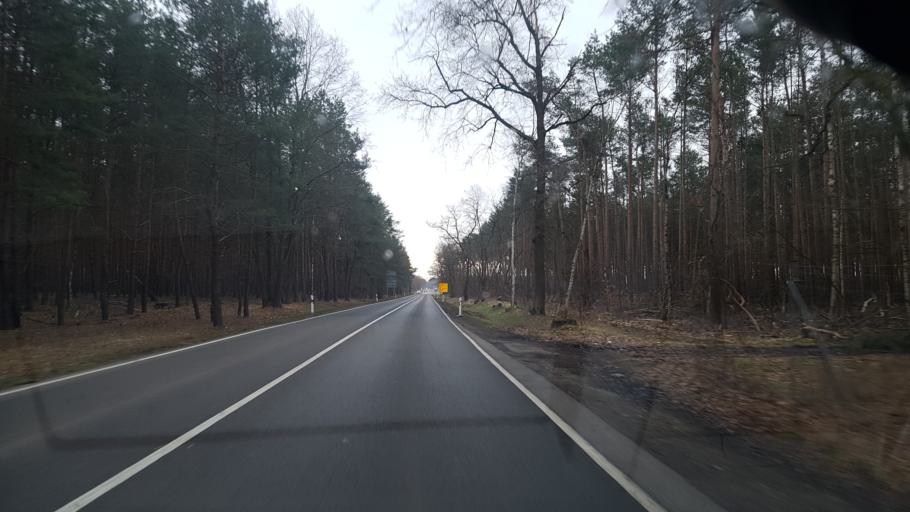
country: DE
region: Brandenburg
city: Heinersbruck
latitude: 51.7109
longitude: 14.4674
